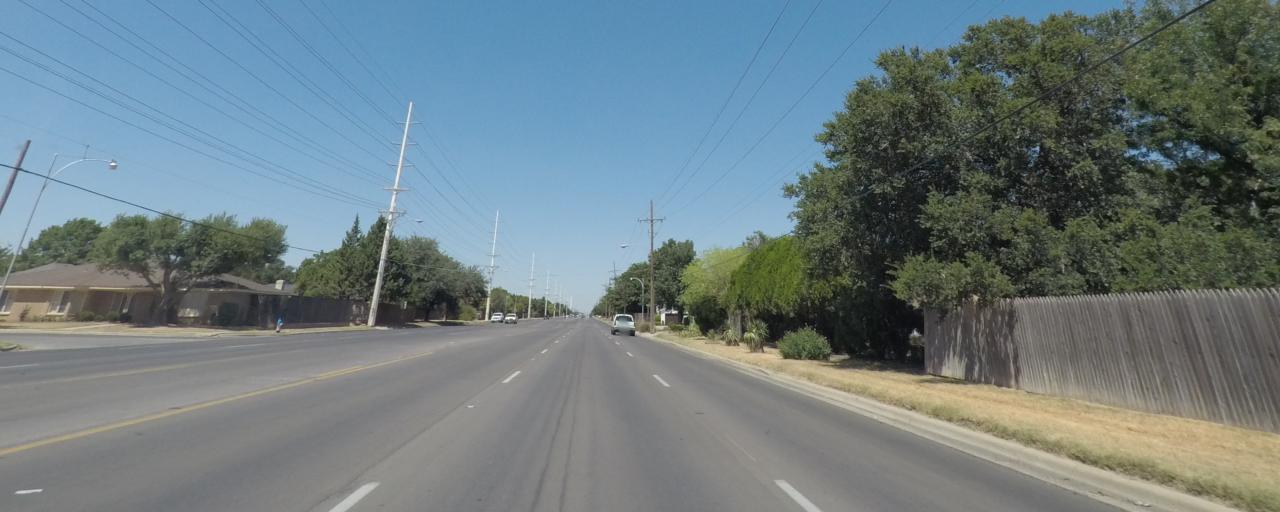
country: US
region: Texas
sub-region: Lubbock County
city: Lubbock
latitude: 33.5105
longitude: -101.8876
